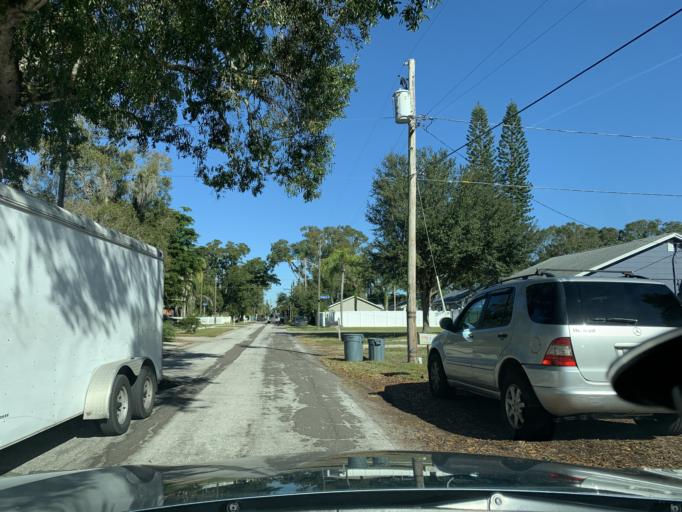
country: US
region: Florida
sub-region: Pinellas County
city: Gulfport
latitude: 27.7539
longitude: -82.7038
